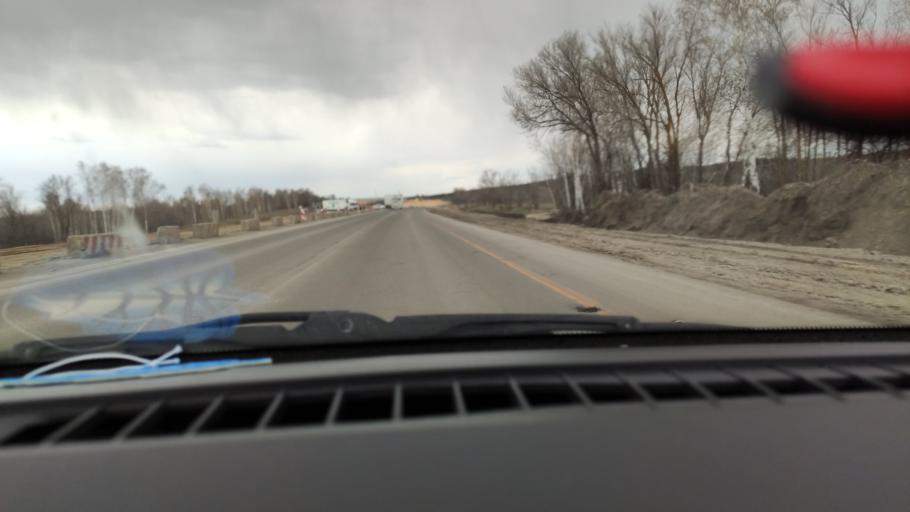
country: RU
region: Saratov
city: Sinodskoye
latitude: 52.0194
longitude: 46.7036
